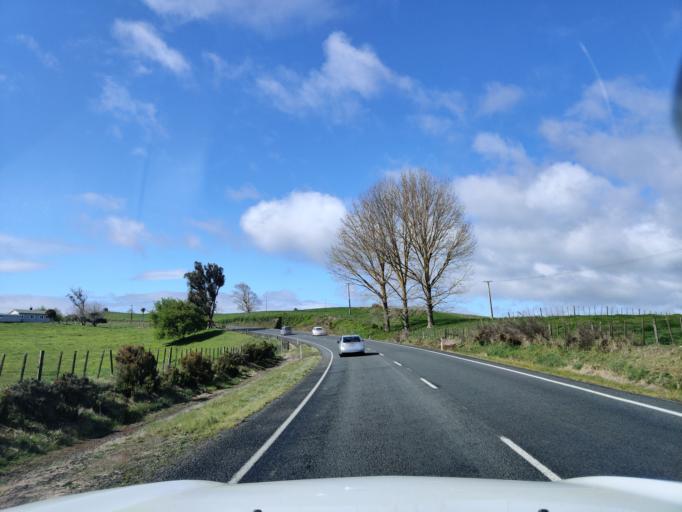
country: NZ
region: Waikato
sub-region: Otorohanga District
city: Otorohanga
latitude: -38.0933
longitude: 175.1826
